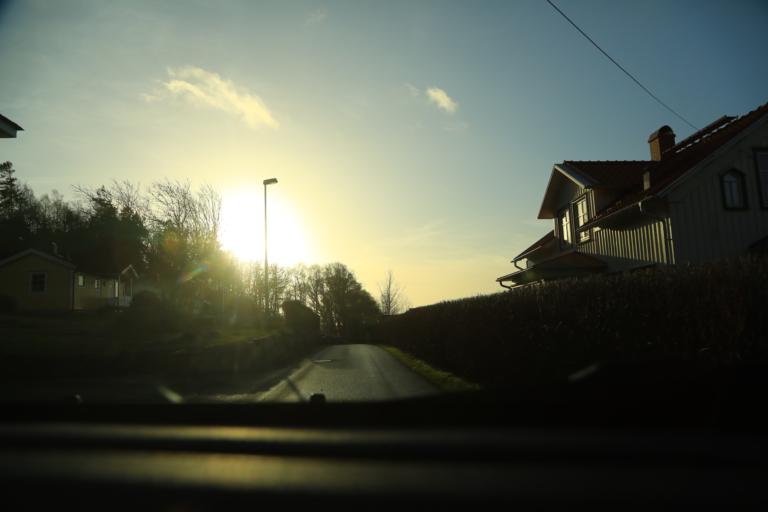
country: SE
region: Halland
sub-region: Varbergs Kommun
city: Varberg
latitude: 57.1911
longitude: 12.2155
